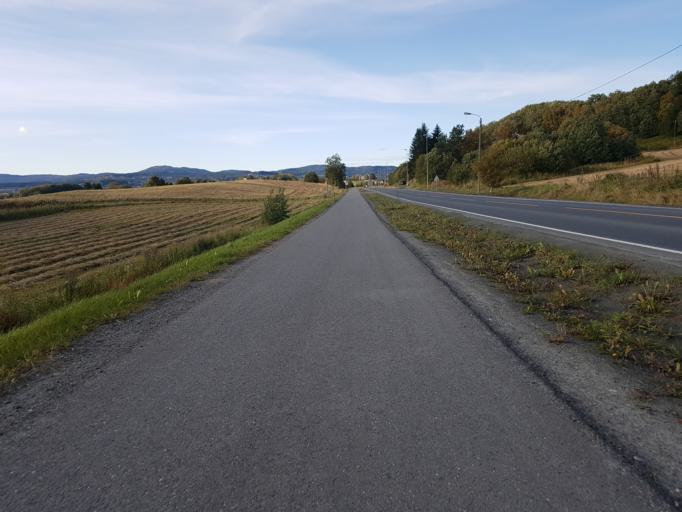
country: NO
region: Sor-Trondelag
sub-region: Trondheim
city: Trondheim
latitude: 63.3712
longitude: 10.4350
